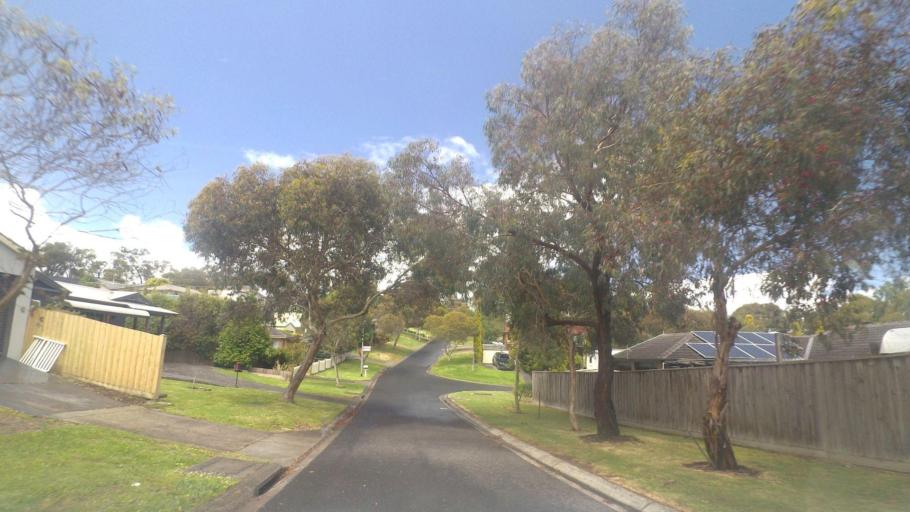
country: AU
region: Victoria
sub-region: Yarra Ranges
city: Mount Evelyn
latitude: -37.7663
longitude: 145.3676
